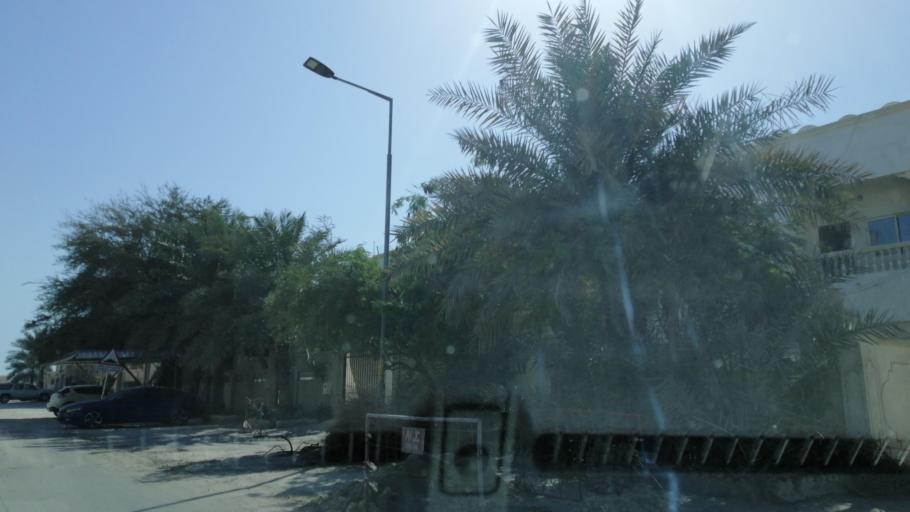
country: BH
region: Muharraq
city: Al Hadd
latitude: 26.2474
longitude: 50.6369
